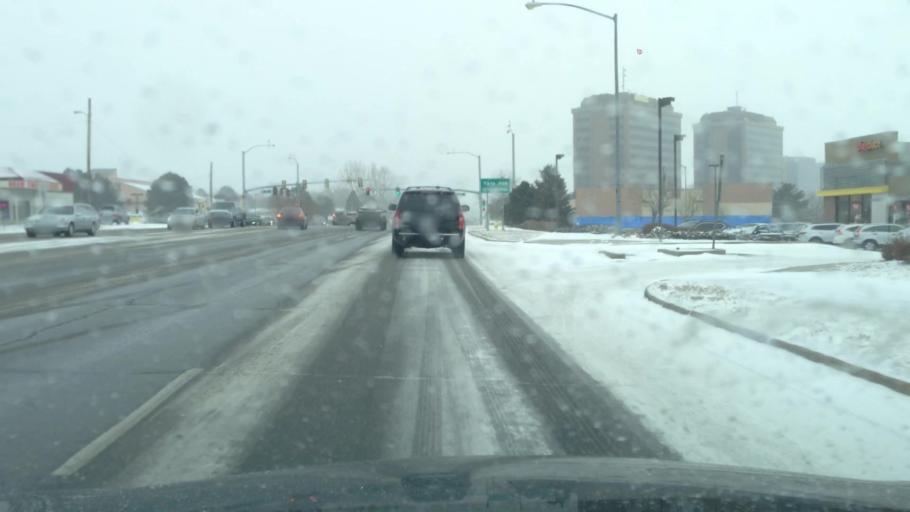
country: US
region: Colorado
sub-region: Adams County
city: Aurora
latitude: 39.6685
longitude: -104.8634
